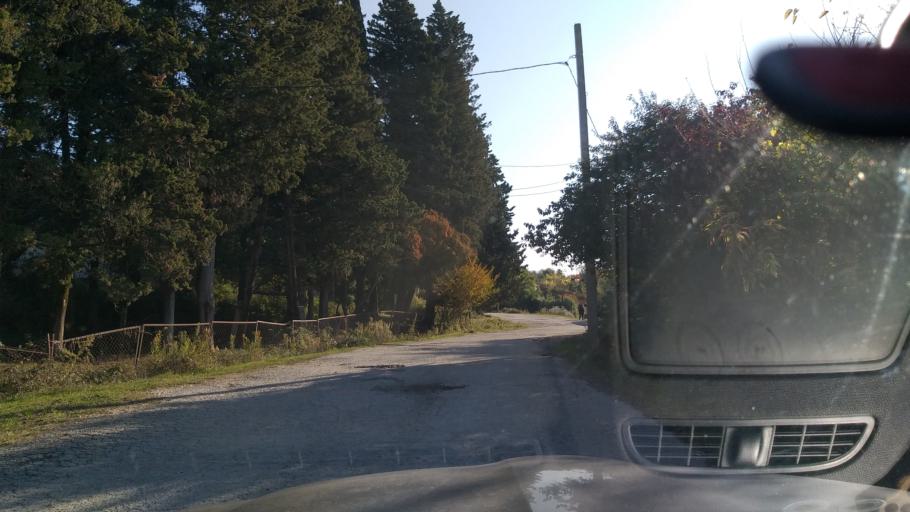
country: GE
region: Abkhazia
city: Stantsiya Novyy Afon
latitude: 43.0646
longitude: 40.8839
